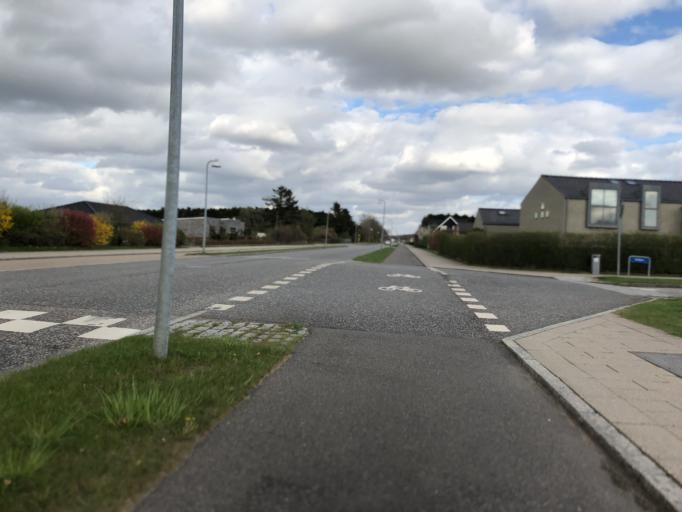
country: DK
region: Zealand
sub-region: Ringsted Kommune
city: Ringsted
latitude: 55.4507
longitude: 11.8058
